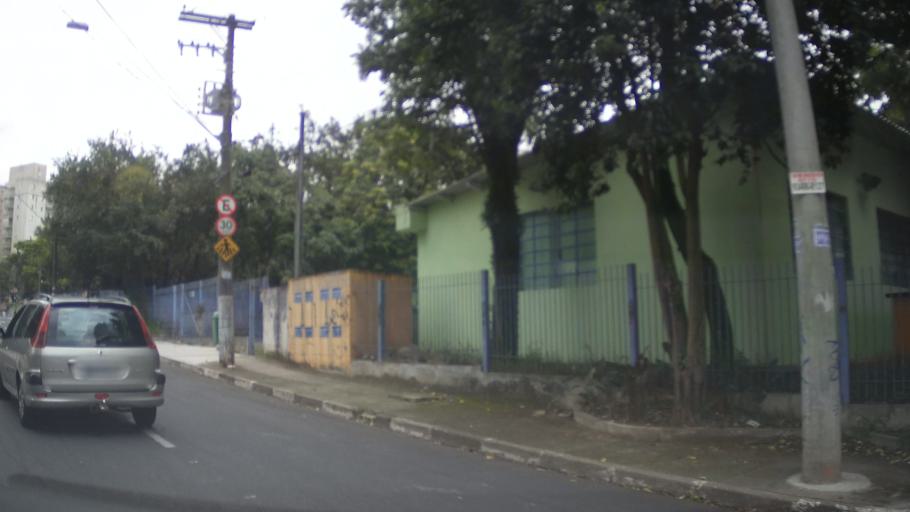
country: BR
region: Sao Paulo
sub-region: Guarulhos
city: Guarulhos
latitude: -23.4627
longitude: -46.5138
